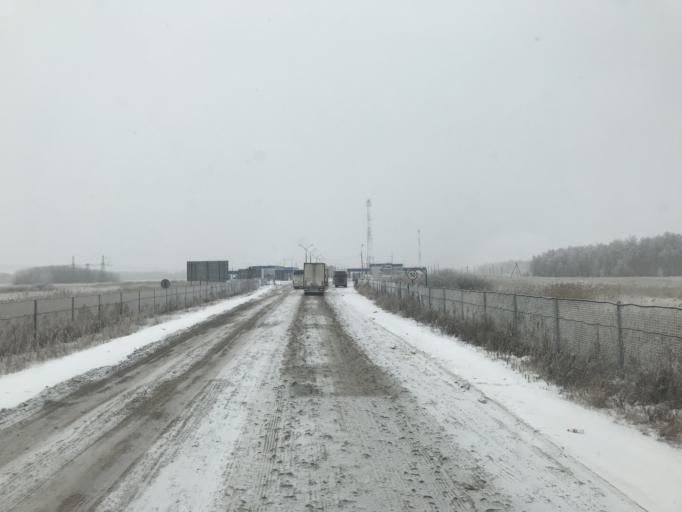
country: RU
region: Kurgan
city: Petukhovo
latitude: 55.0915
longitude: 68.2489
